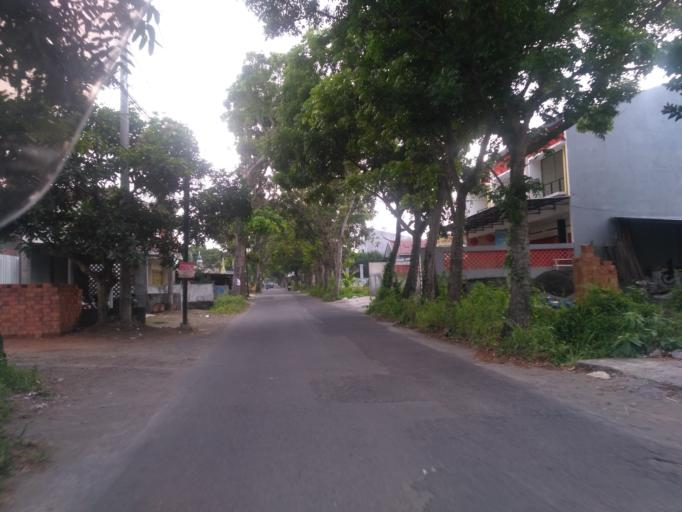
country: ID
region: Daerah Istimewa Yogyakarta
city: Yogyakarta
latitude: -7.7726
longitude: 110.3427
